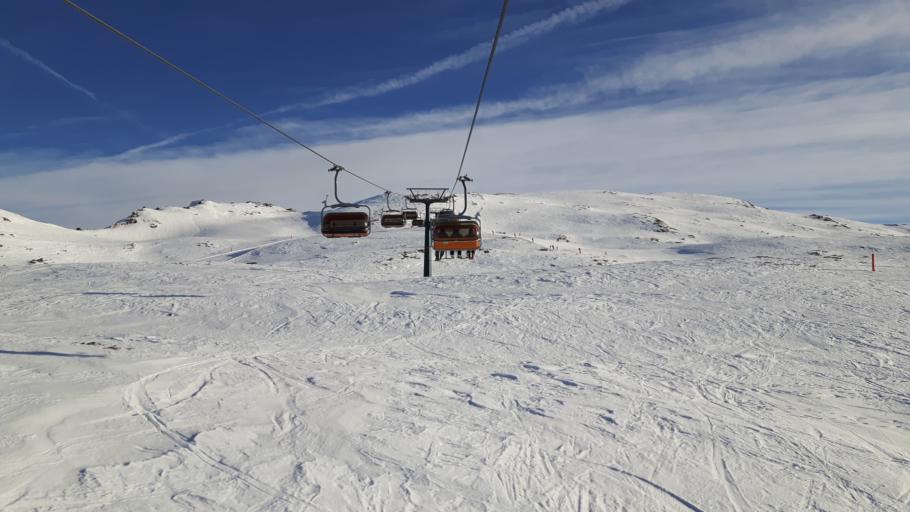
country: IT
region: Trentino-Alto Adige
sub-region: Provincia di Trento
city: Moena
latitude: 46.3420
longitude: 11.7167
